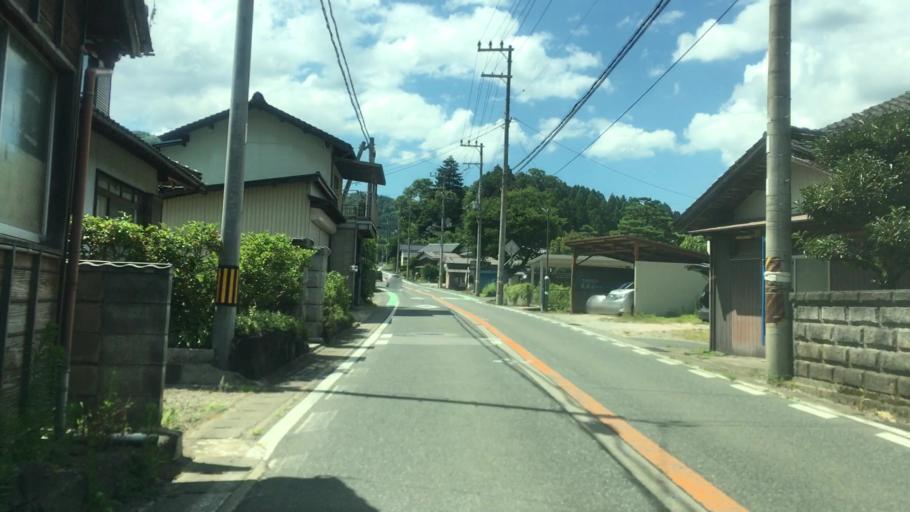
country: JP
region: Hyogo
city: Toyooka
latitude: 35.4730
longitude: 134.7160
